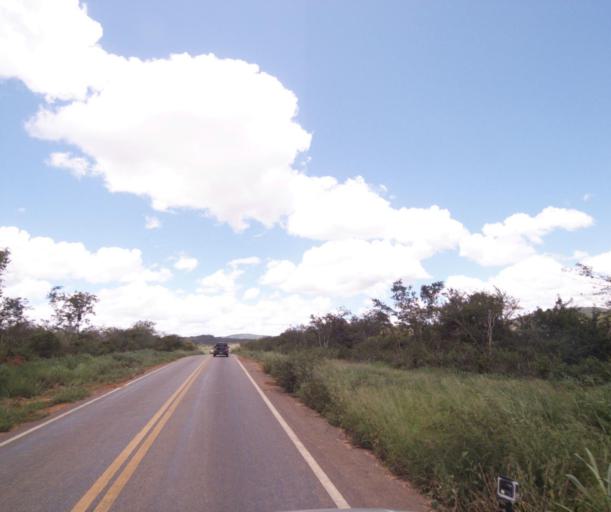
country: BR
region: Bahia
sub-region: Pocoes
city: Pocoes
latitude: -14.3861
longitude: -40.5173
